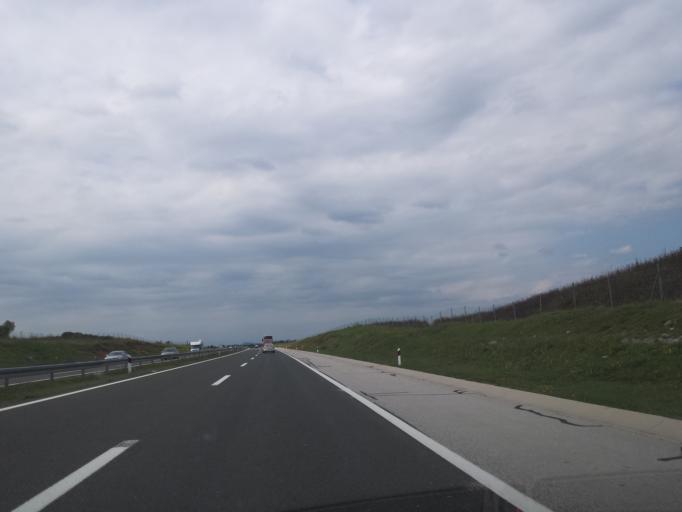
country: HR
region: Zadarska
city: Starigrad
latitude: 44.4681
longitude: 15.5944
